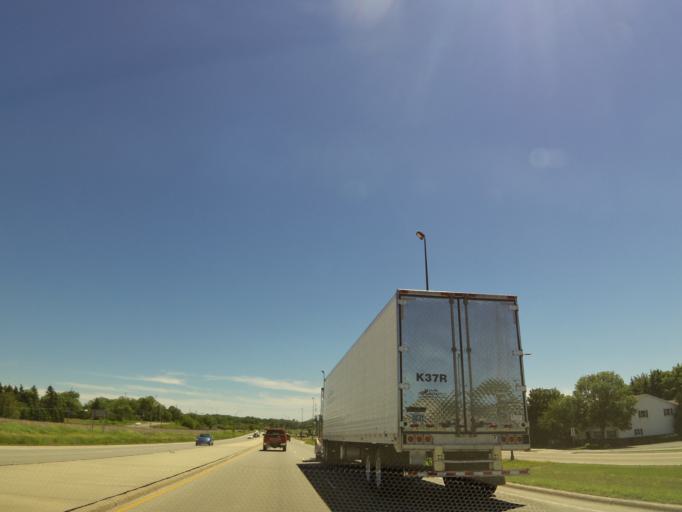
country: US
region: Minnesota
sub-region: Becker County
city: Detroit Lakes
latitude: 46.8085
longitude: -95.8216
